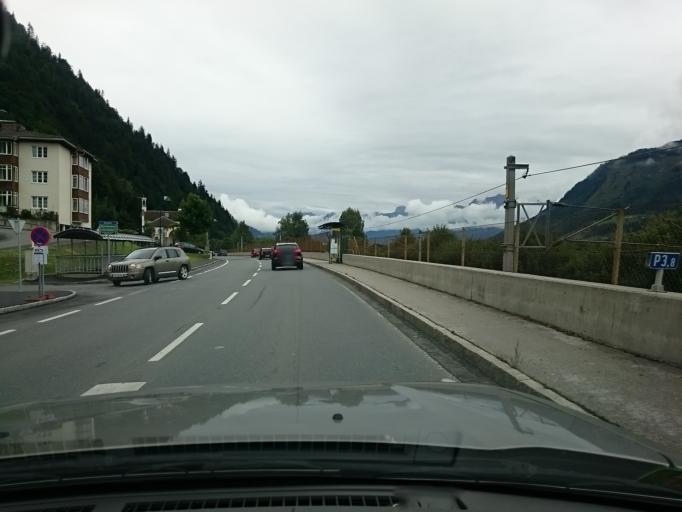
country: AT
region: Salzburg
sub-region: Politischer Bezirk Zell am See
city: Zell am See
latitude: 47.3346
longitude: 12.7977
